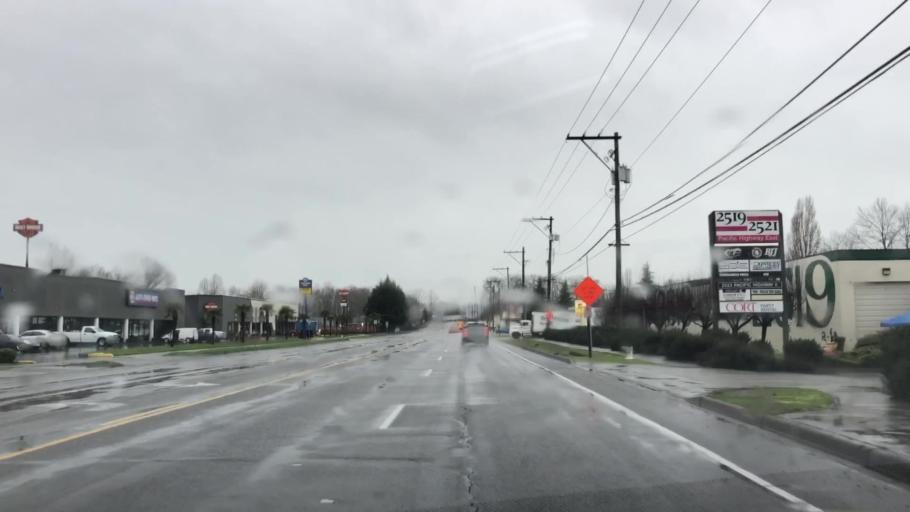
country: US
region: Washington
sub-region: Pierce County
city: Fife
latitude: 47.2433
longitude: -122.3949
